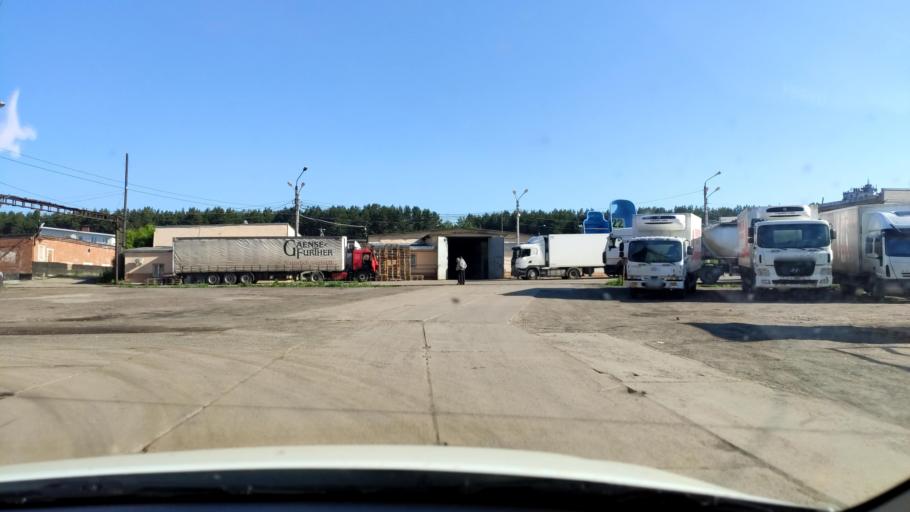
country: RU
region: Tatarstan
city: Staroye Arakchino
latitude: 55.8407
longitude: 49.0434
